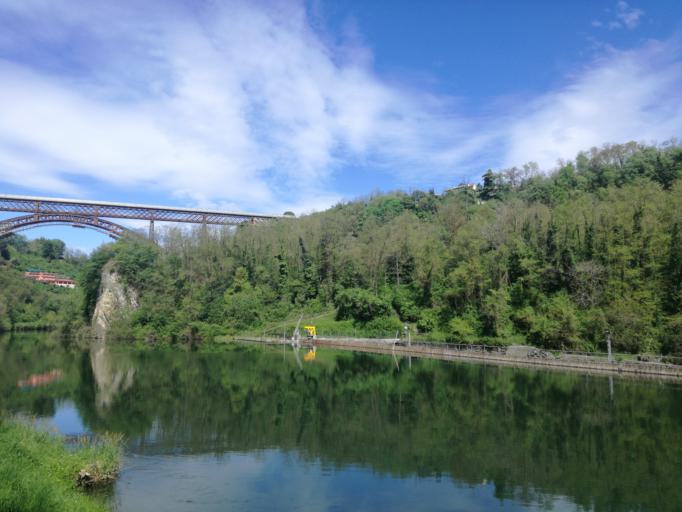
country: IT
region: Lombardy
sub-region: Provincia di Lecco
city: Paderno d'Adda
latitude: 45.6804
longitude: 9.4563
